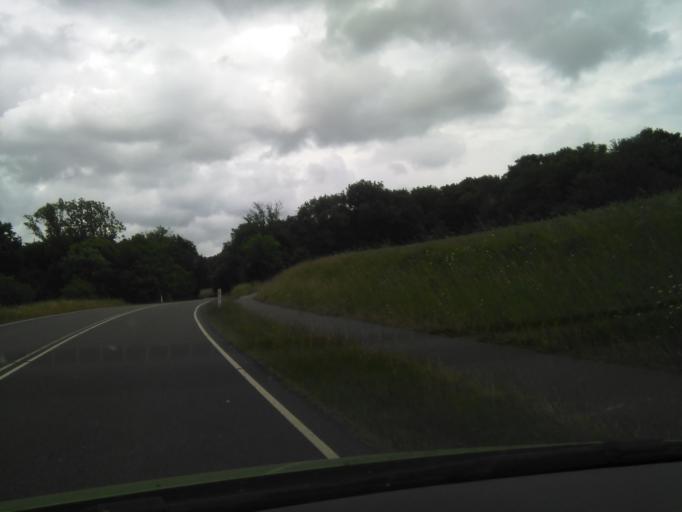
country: DK
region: Capital Region
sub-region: Bornholm Kommune
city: Akirkeby
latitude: 55.2324
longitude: 14.8770
